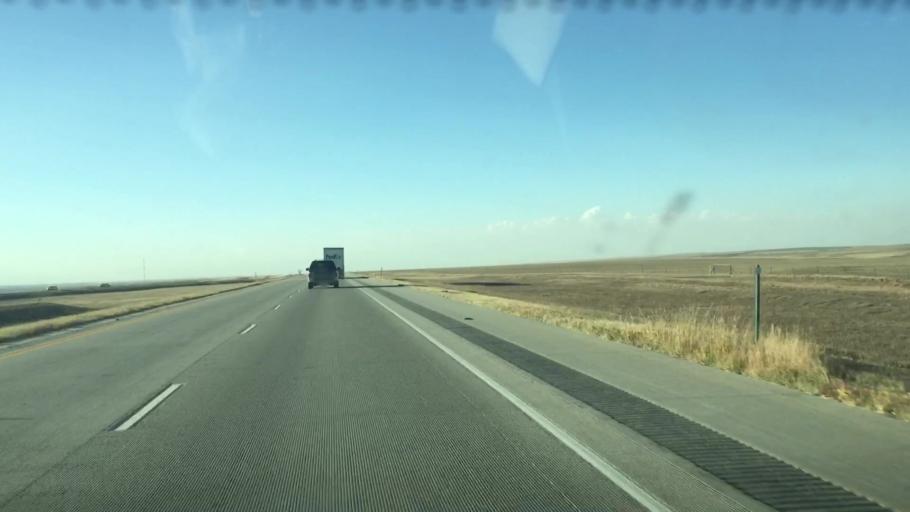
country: US
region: Colorado
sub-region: Lincoln County
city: Limon
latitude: 39.4174
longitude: -103.9054
